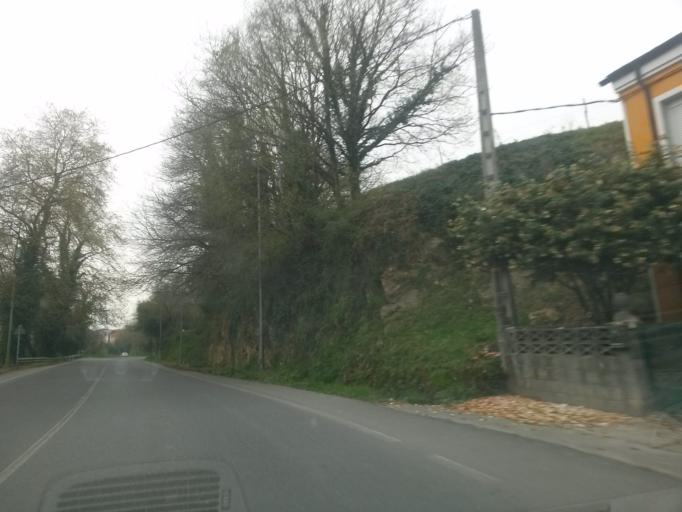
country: ES
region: Galicia
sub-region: Provincia de Lugo
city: Lugo
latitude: 43.0236
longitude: -7.5466
